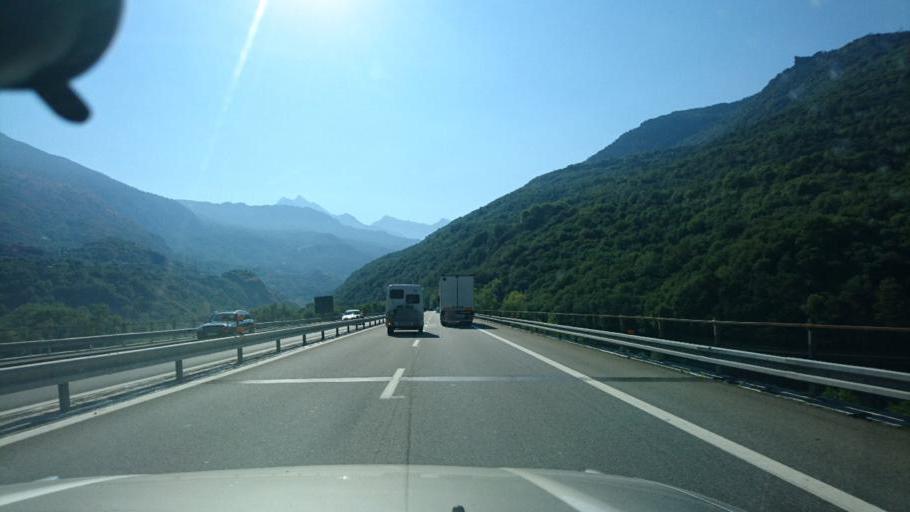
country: IT
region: Aosta Valley
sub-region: Valle d'Aosta
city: Saint-Vincent
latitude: 45.7440
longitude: 7.6359
